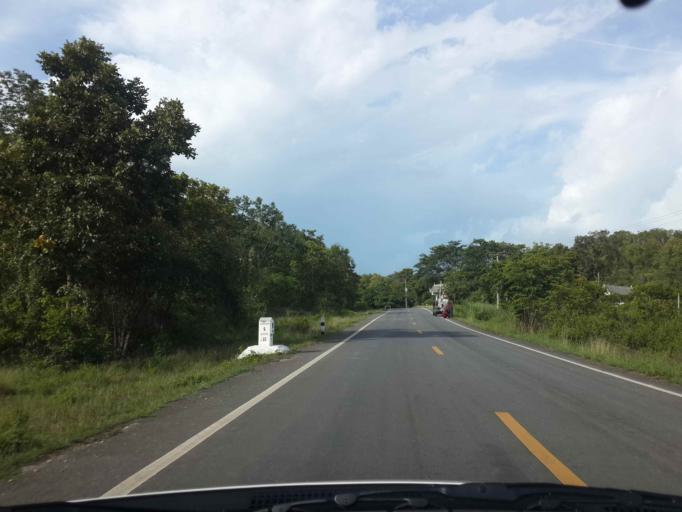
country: TH
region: Kanchanaburi
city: Dan Makham Tia
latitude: 13.8255
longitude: 99.1675
